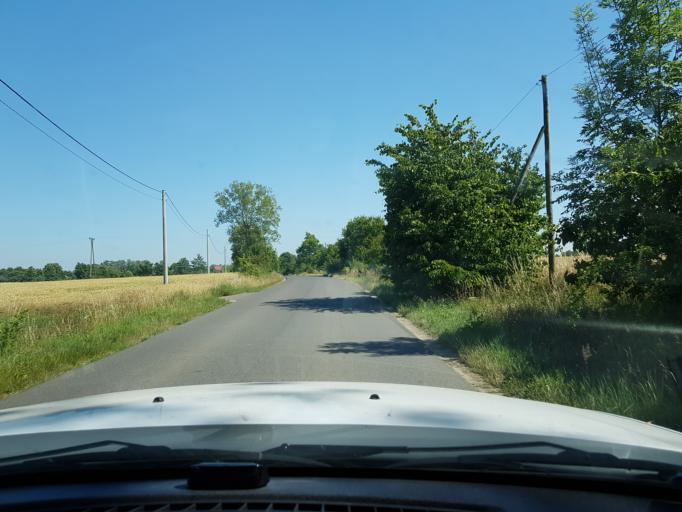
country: PL
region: West Pomeranian Voivodeship
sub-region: Powiat koszalinski
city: Mielno
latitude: 54.1891
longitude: 16.0615
